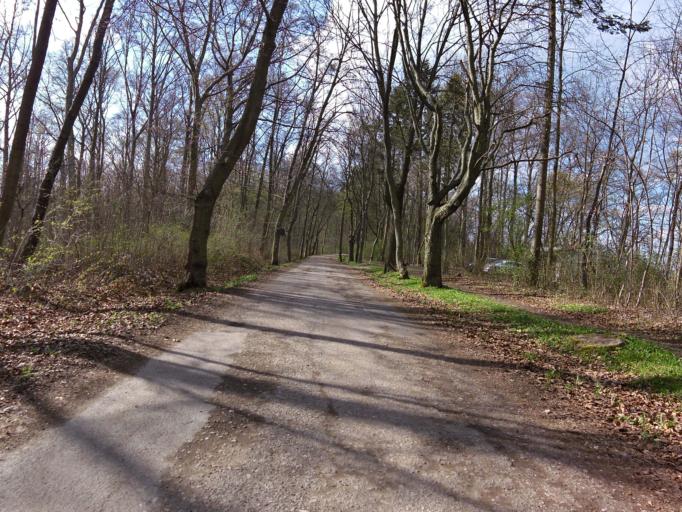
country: DE
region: Thuringia
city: Gotha
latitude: 50.9563
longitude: 10.6828
